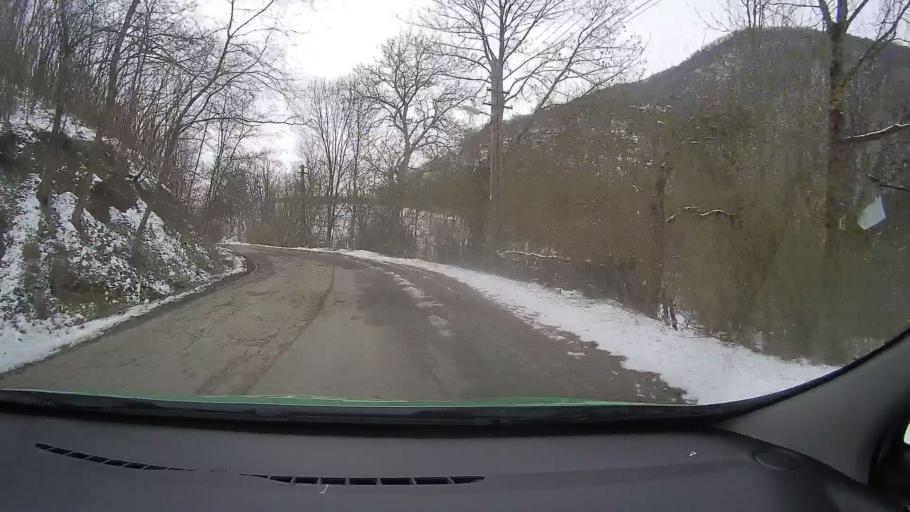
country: RO
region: Hunedoara
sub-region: Comuna Balsa
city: Balsa
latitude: 46.0190
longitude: 23.1463
